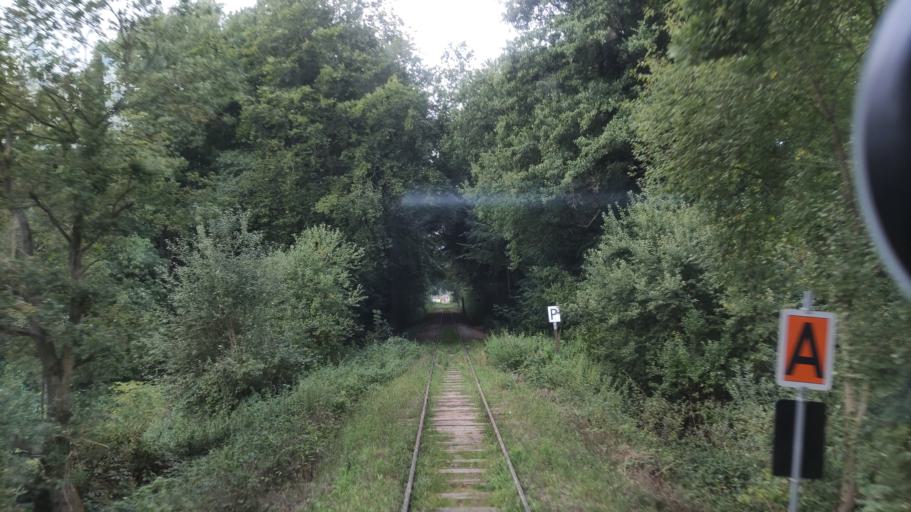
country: DE
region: Lower Saxony
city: Scharnebeck
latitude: 53.2872
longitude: 10.5149
